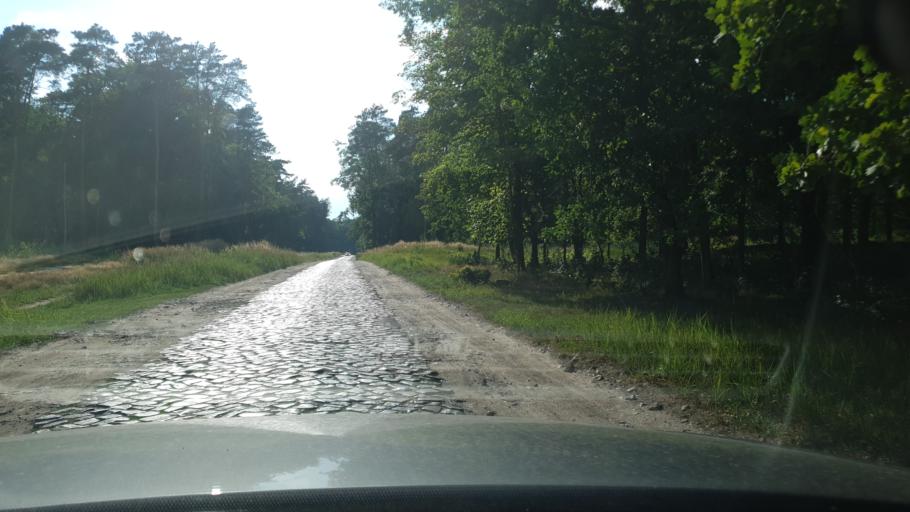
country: PL
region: Kujawsko-Pomorskie
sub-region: Grudziadz
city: Grudziadz
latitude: 53.4415
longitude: 18.7618
